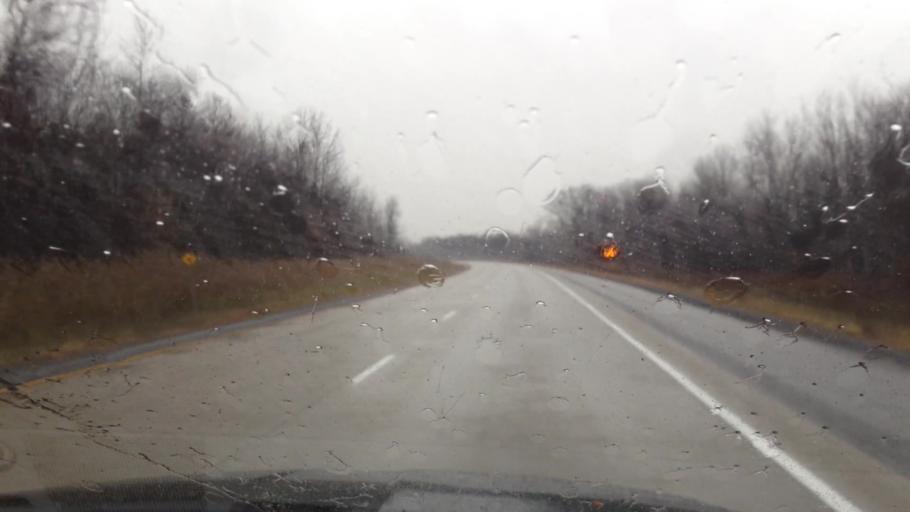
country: CA
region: Ontario
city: Hawkesbury
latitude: 45.4482
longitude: -74.7131
